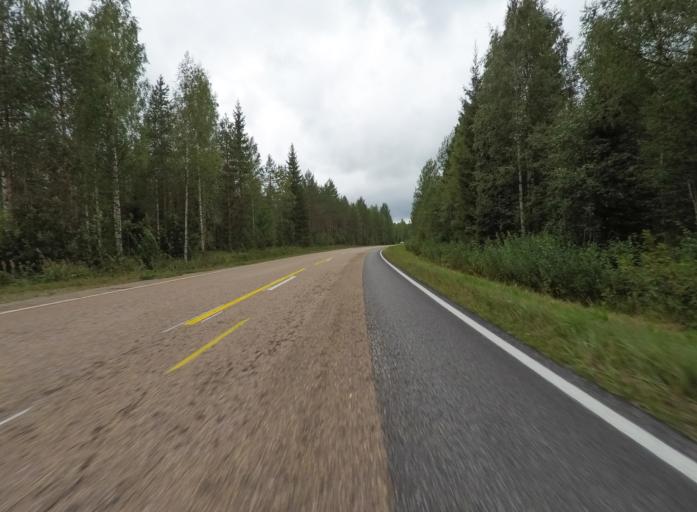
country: FI
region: Central Finland
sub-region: Jyvaeskylae
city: Hankasalmi
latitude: 62.3606
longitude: 26.5341
